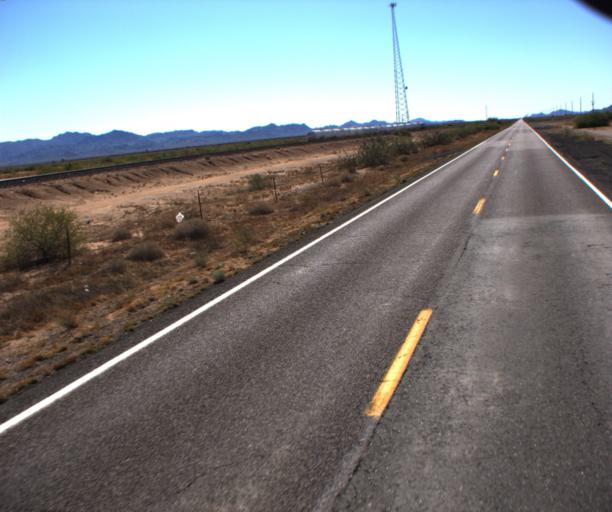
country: US
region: Arizona
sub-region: La Paz County
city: Salome
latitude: 33.8402
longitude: -113.8893
